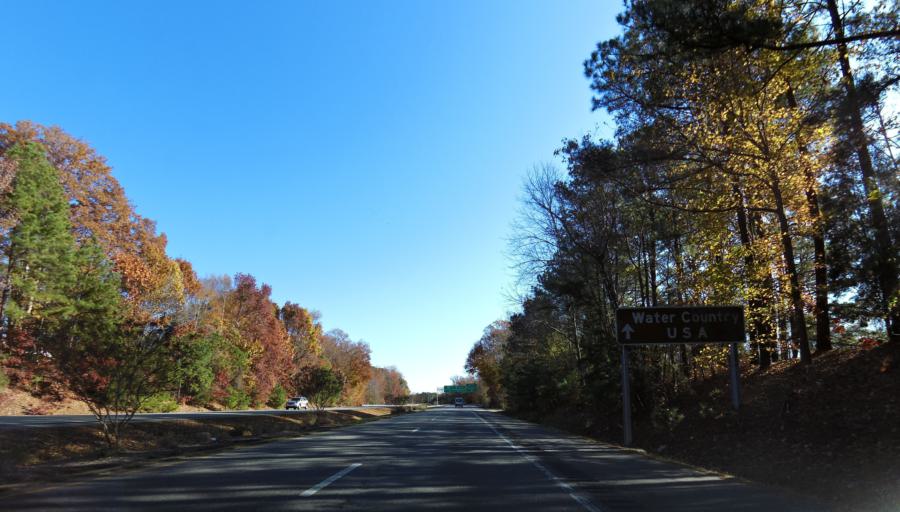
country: US
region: Virginia
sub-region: City of Williamsburg
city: Williamsburg
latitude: 37.2551
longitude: -76.6522
